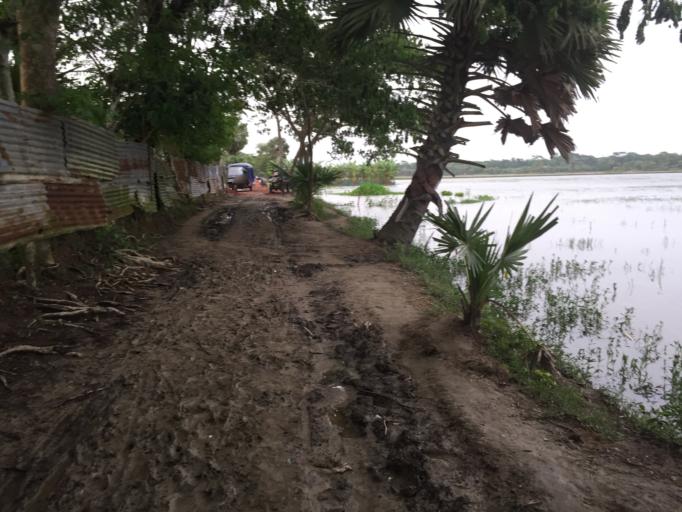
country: BD
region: Barisal
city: Mathba
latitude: 22.1925
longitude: 89.9314
